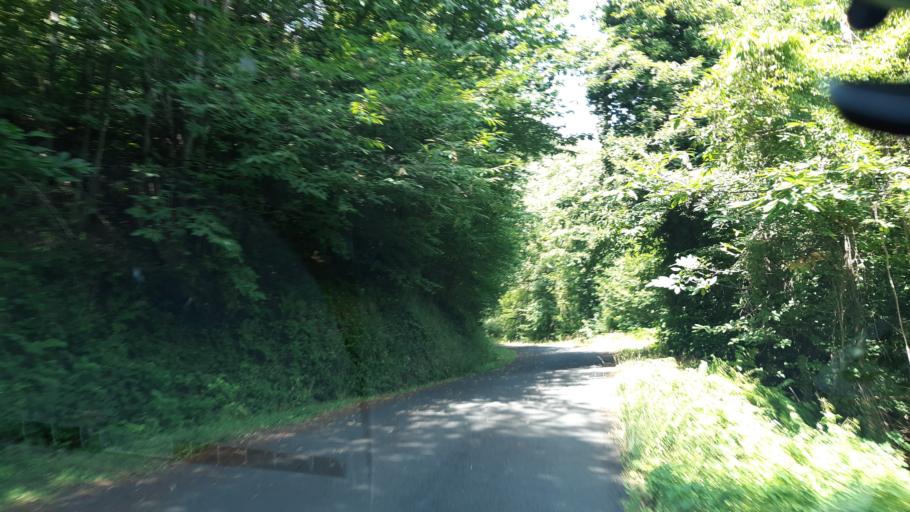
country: FR
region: Languedoc-Roussillon
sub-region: Departement des Pyrenees-Orientales
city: Arles
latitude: 42.5349
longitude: 2.5870
